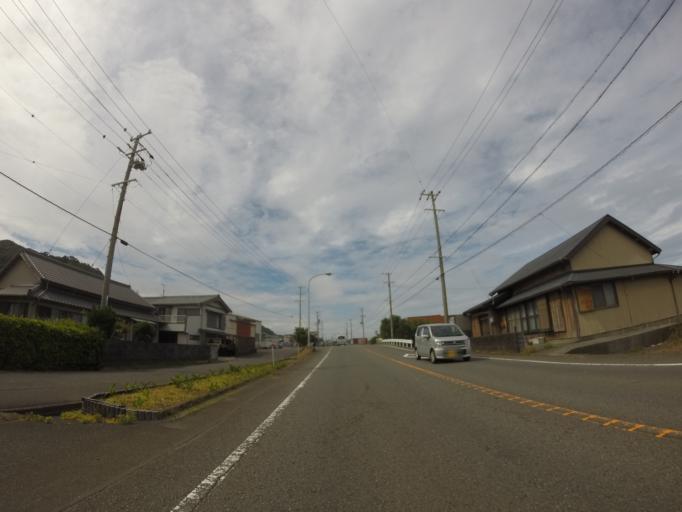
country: JP
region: Shizuoka
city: Sagara
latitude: 34.7063
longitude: 138.2131
